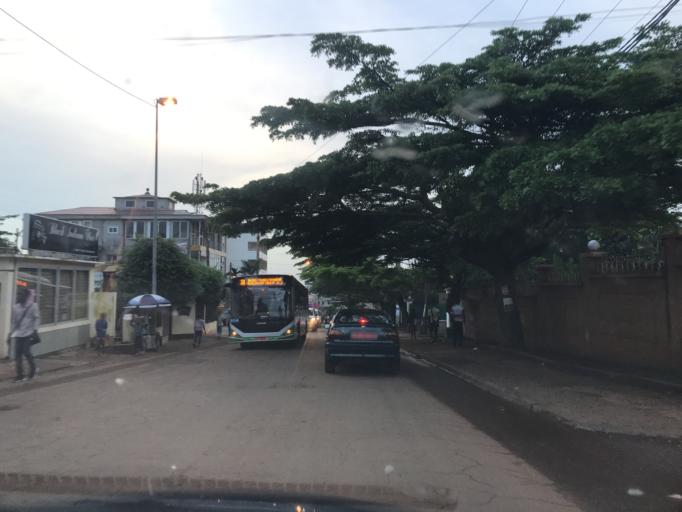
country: CM
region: Centre
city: Yaounde
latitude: 3.8773
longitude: 11.5247
